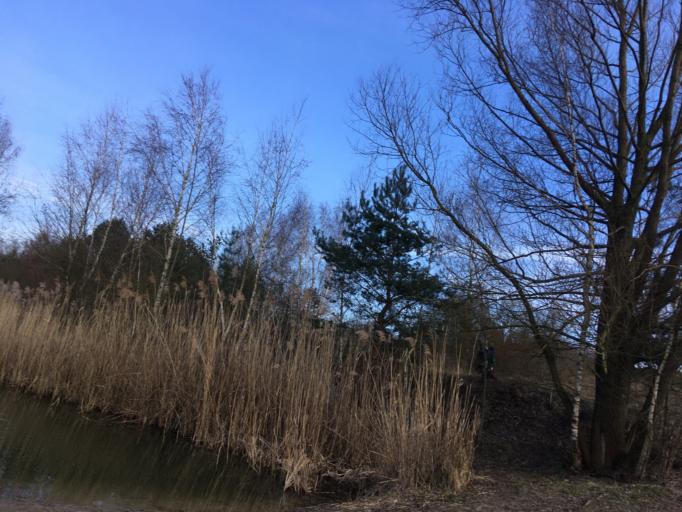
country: DE
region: Berlin
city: Blankenfelde
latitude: 52.6325
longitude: 13.4067
